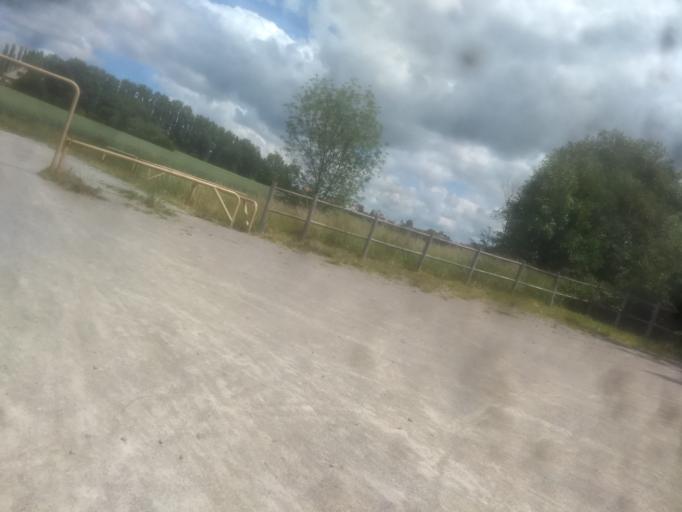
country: FR
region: Nord-Pas-de-Calais
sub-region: Departement du Pas-de-Calais
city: Maroeuil
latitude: 50.3177
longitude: 2.7076
